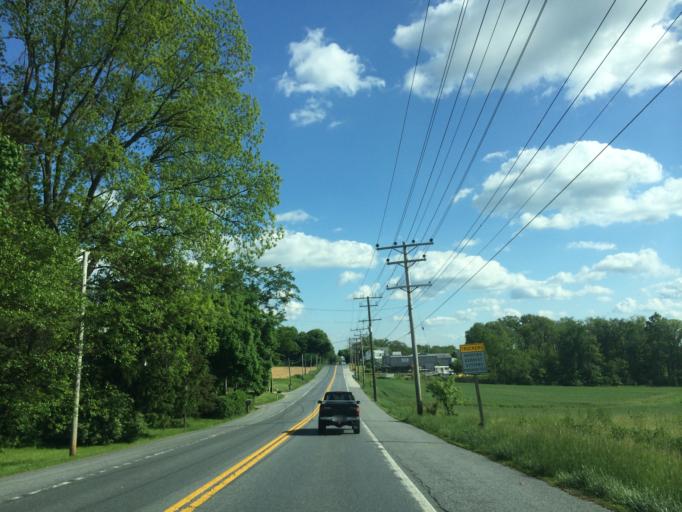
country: US
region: Maryland
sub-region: Carroll County
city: Hampstead
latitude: 39.5731
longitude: -76.8405
